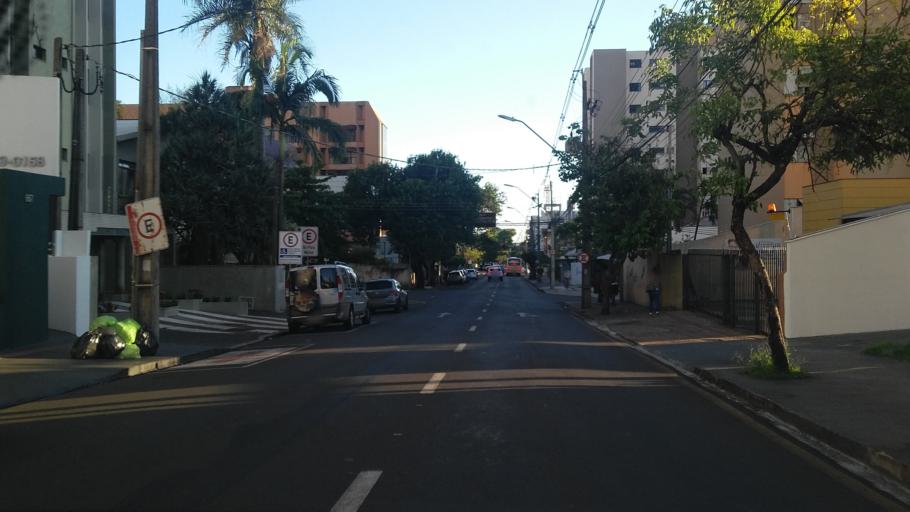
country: BR
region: Parana
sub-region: Londrina
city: Londrina
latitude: -23.3182
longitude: -51.1576
